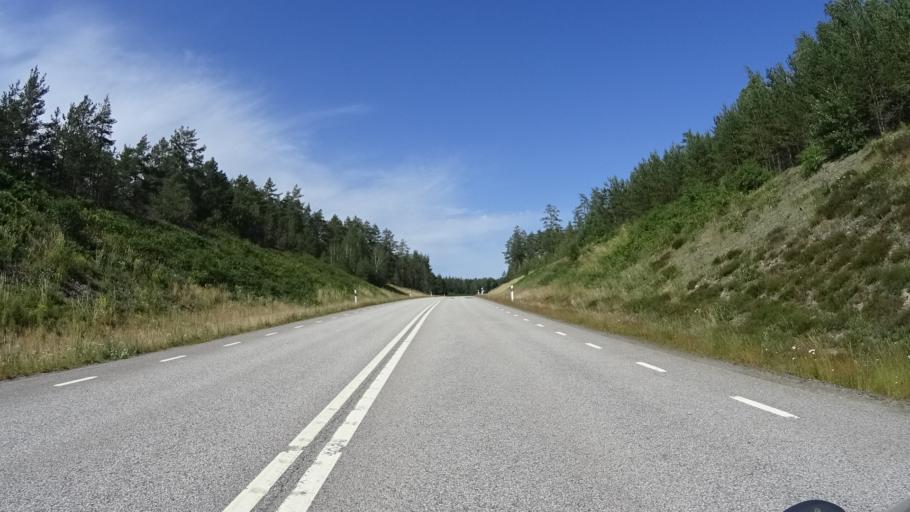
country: SE
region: Kalmar
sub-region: Vasterviks Kommun
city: Gamleby
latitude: 57.9237
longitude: 16.3747
